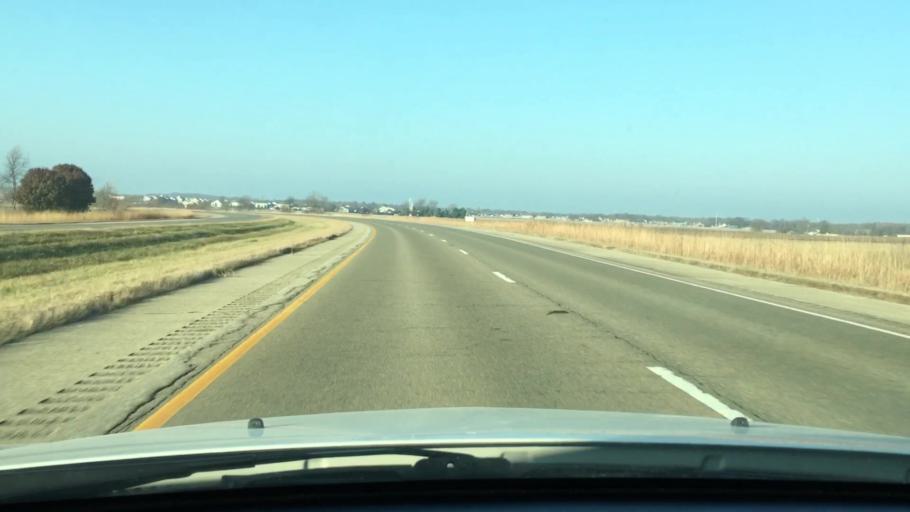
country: US
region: Illinois
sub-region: Tazewell County
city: Washington
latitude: 40.7276
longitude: -89.4195
